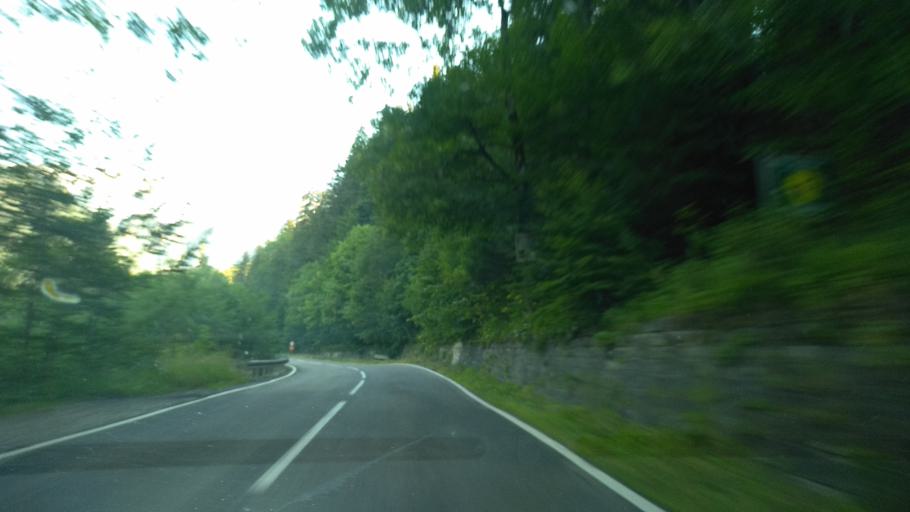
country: RO
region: Prahova
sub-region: Oras Sinaia
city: Sinaia
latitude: 45.3272
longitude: 25.5248
